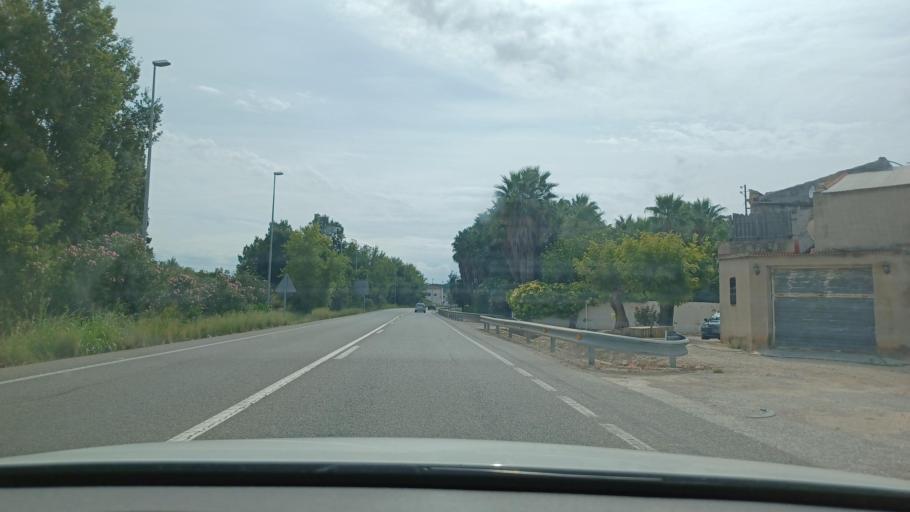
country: ES
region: Catalonia
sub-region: Provincia de Tarragona
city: Tortosa
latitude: 40.7846
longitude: 0.5019
